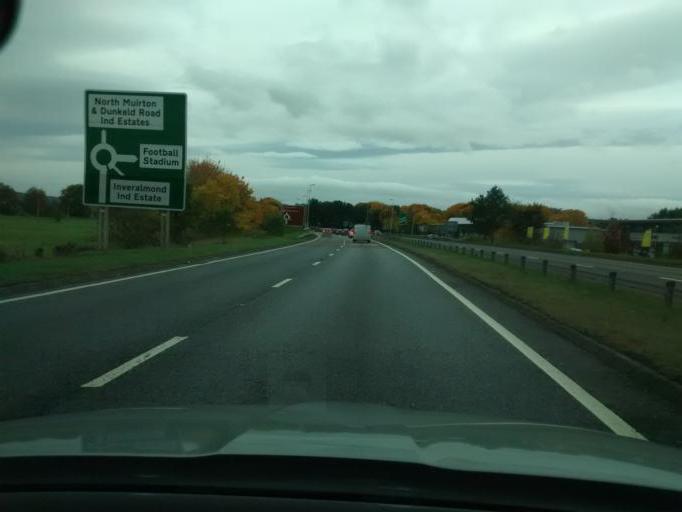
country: GB
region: Scotland
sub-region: Perth and Kinross
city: Luncarty
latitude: 56.4220
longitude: -3.4665
